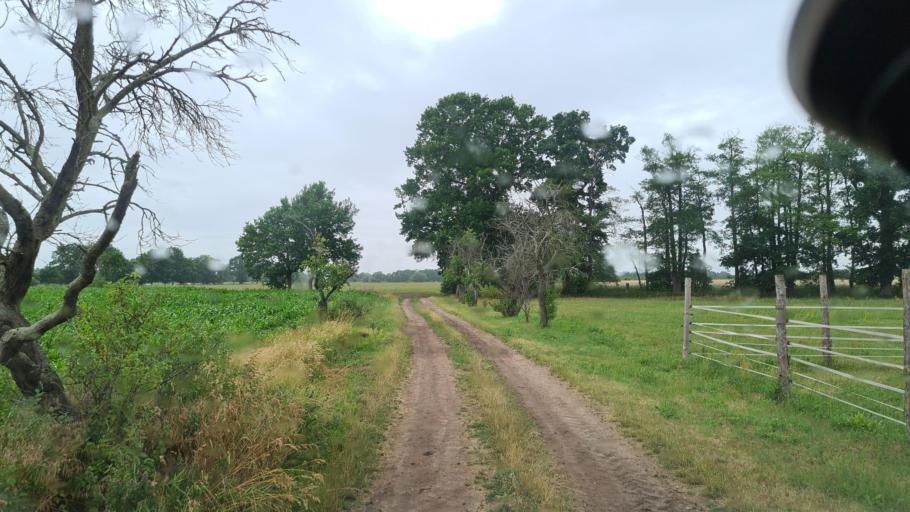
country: DE
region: Saxony-Anhalt
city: Holzdorf
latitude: 51.8175
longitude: 13.1609
